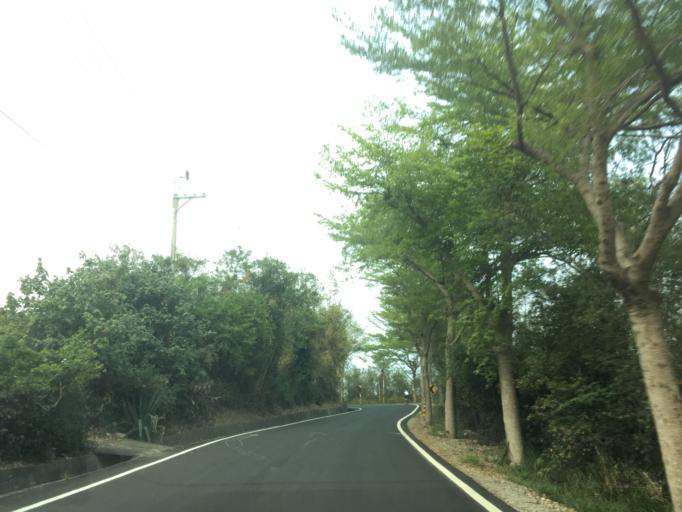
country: TW
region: Taiwan
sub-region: Taitung
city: Taitung
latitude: 22.7897
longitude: 121.1613
